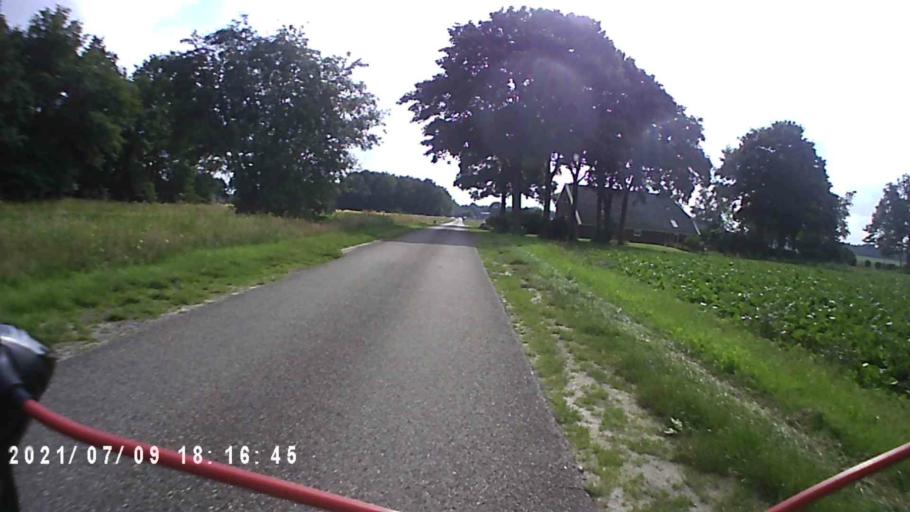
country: NL
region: Groningen
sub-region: Gemeente Pekela
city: Oude Pekela
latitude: 53.0542
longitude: 7.0139
